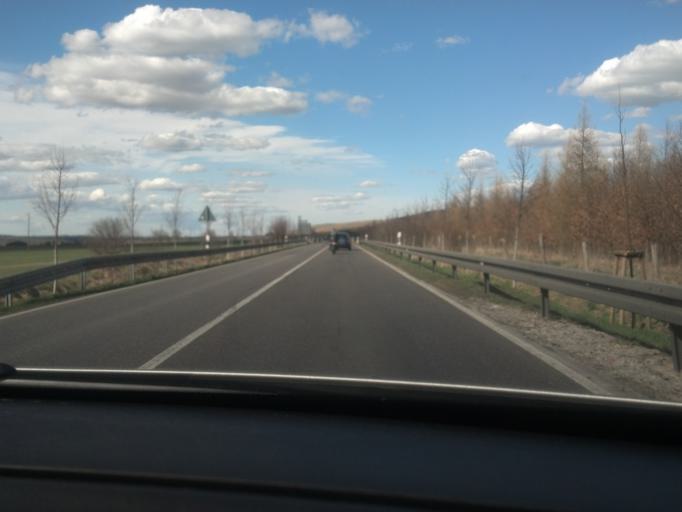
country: DE
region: Mecklenburg-Vorpommern
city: Trollenhagen
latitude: 53.6037
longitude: 13.2692
